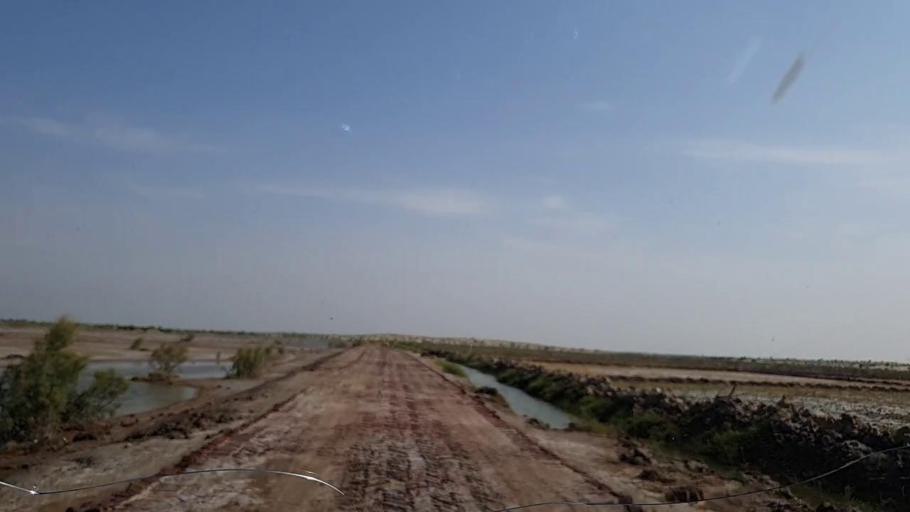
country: PK
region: Sindh
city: Khanpur
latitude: 27.6836
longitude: 69.3680
